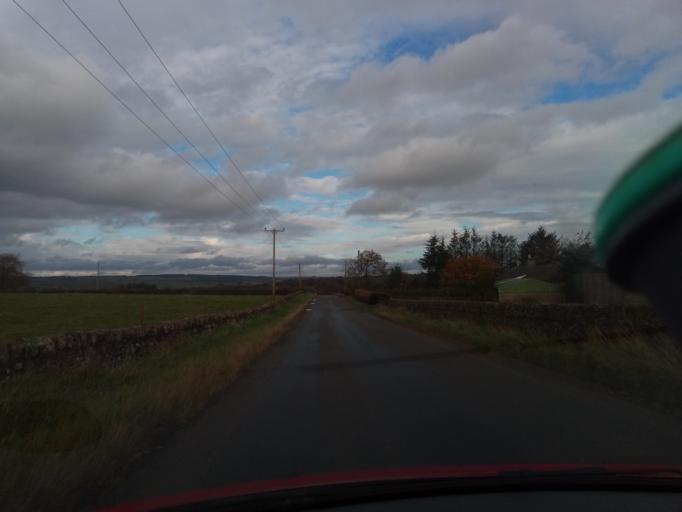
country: GB
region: Scotland
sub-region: South Lanarkshire
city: Carnwath
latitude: 55.7274
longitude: -3.6037
